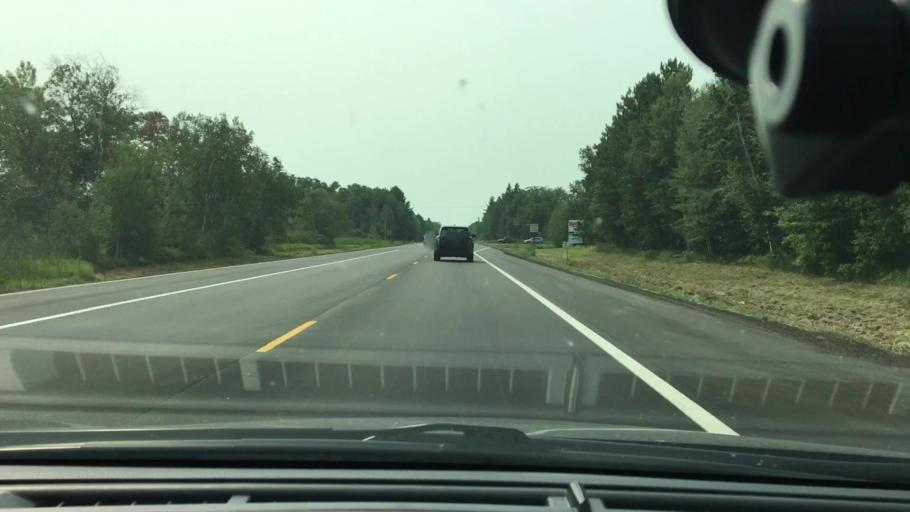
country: US
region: Minnesota
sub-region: Crow Wing County
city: Brainerd
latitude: 46.4519
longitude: -94.1722
